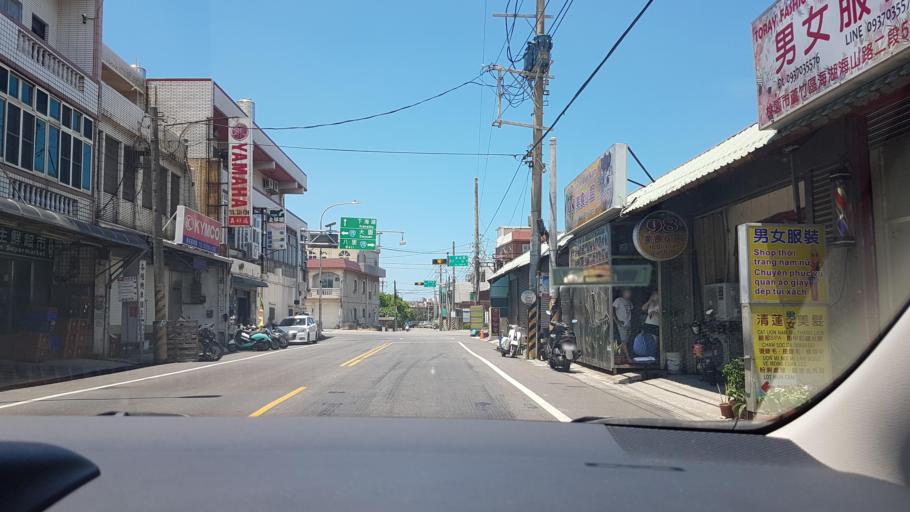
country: TW
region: Taiwan
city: Taoyuan City
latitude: 25.1112
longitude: 121.2545
